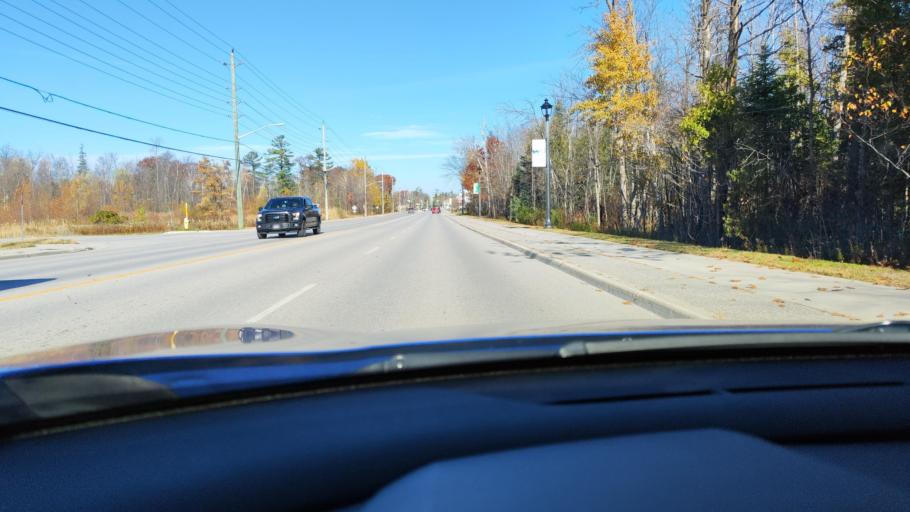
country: CA
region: Ontario
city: Wasaga Beach
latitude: 44.4690
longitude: -80.0749
